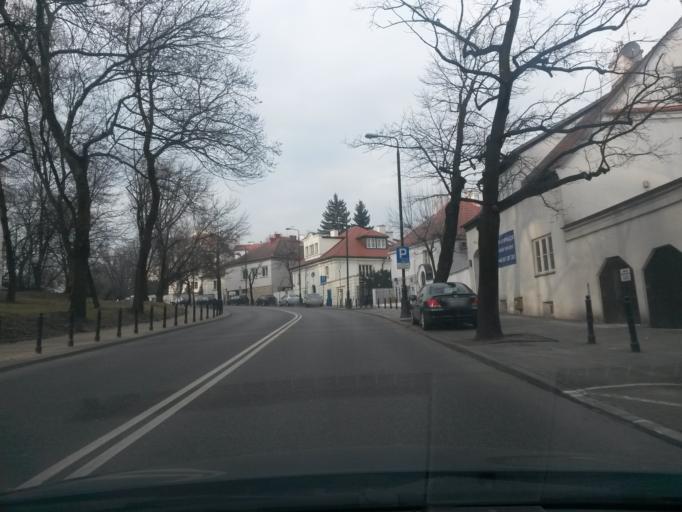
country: PL
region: Masovian Voivodeship
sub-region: Warszawa
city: Srodmiescie
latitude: 52.2234
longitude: 21.0322
